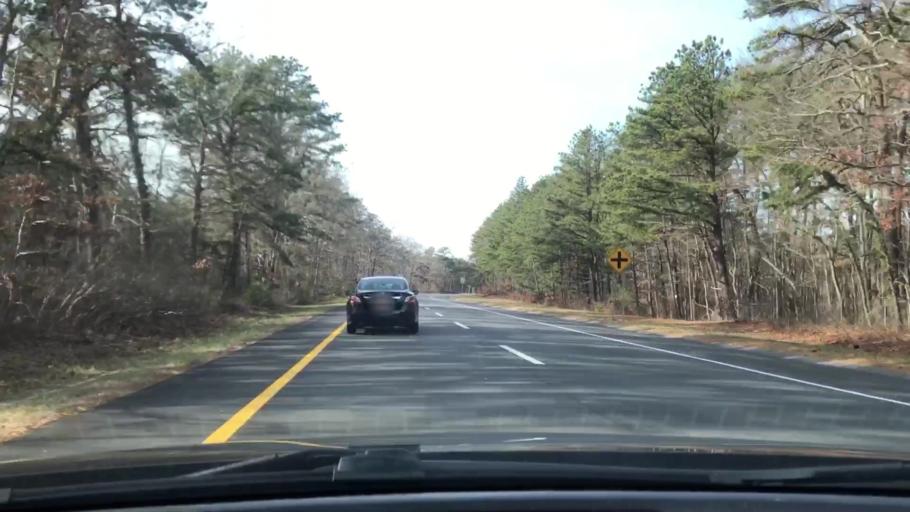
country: US
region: New York
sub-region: Suffolk County
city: Calverton
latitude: 40.9034
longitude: -72.7331
